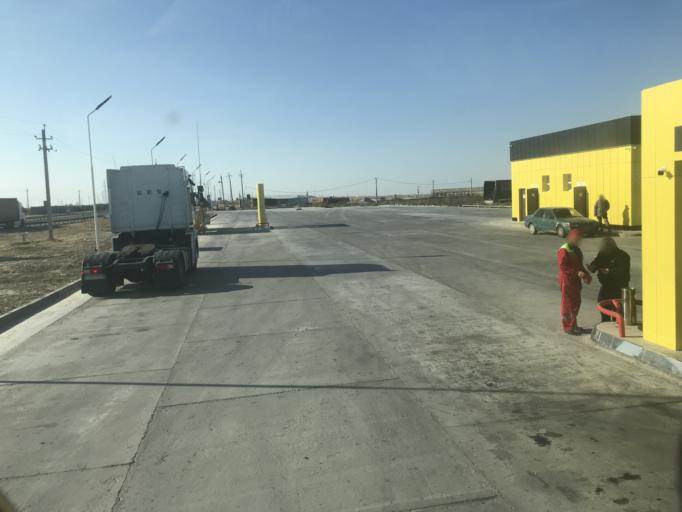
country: KZ
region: Ongtustik Qazaqstan
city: Shymkent
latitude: 42.4504
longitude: 69.6432
